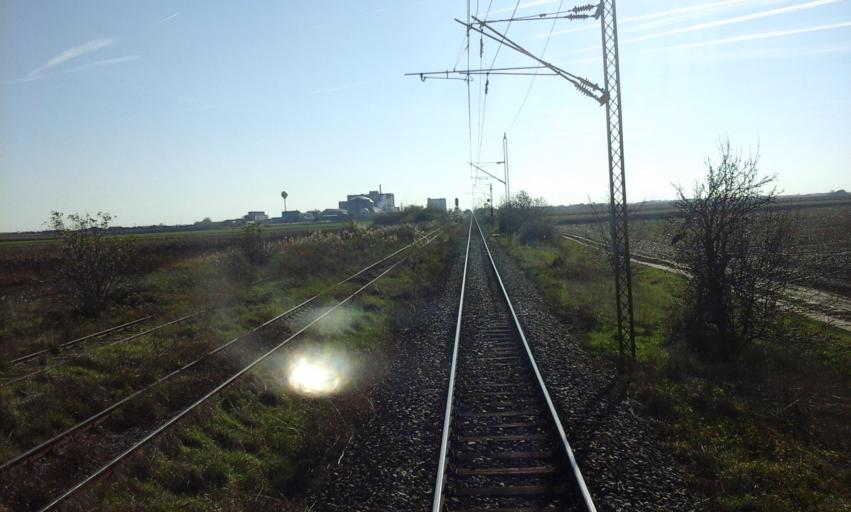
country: RS
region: Autonomna Pokrajina Vojvodina
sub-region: Severnobacki Okrug
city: Subotica
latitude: 46.0177
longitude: 19.6803
